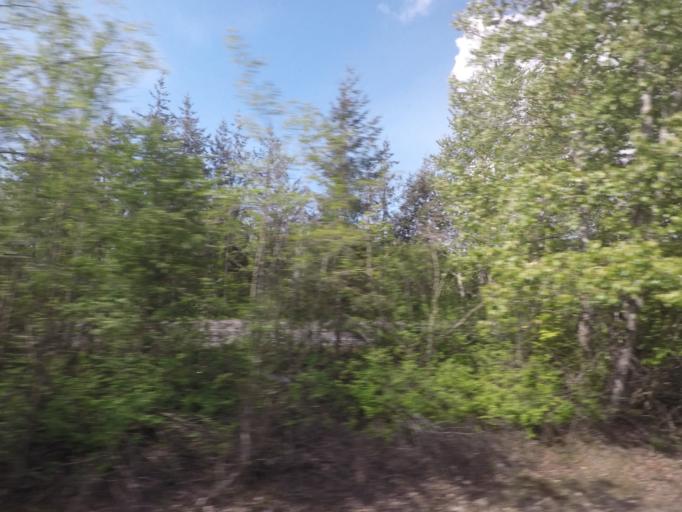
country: US
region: Washington
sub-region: Whatcom County
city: Marietta-Alderwood
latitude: 48.7888
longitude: -122.5605
